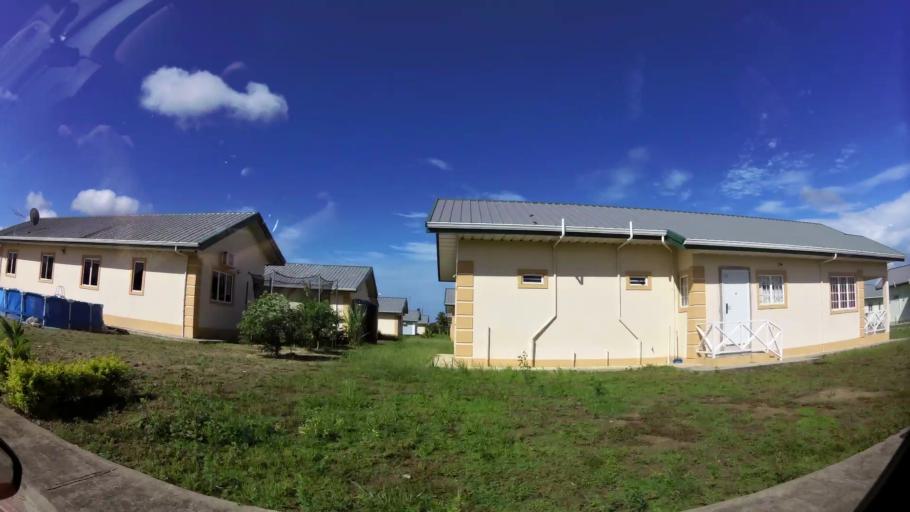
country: TT
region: Chaguanas
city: Chaguanas
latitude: 10.5344
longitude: -61.3963
